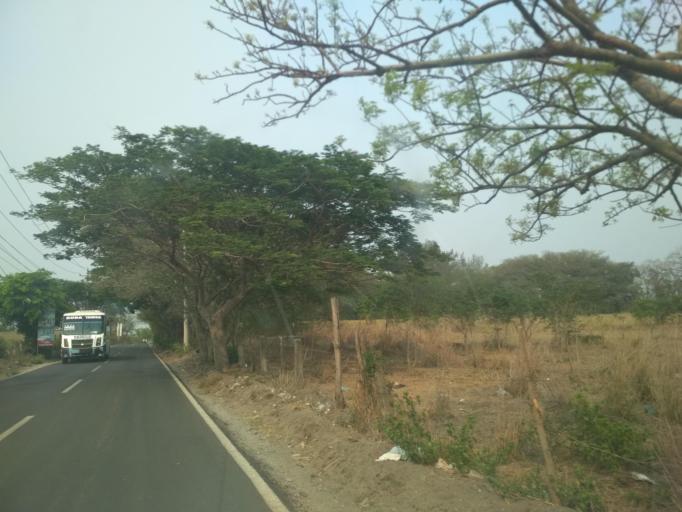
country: MX
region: Veracruz
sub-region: Veracruz
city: Las Amapolas
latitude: 19.1505
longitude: -96.2259
